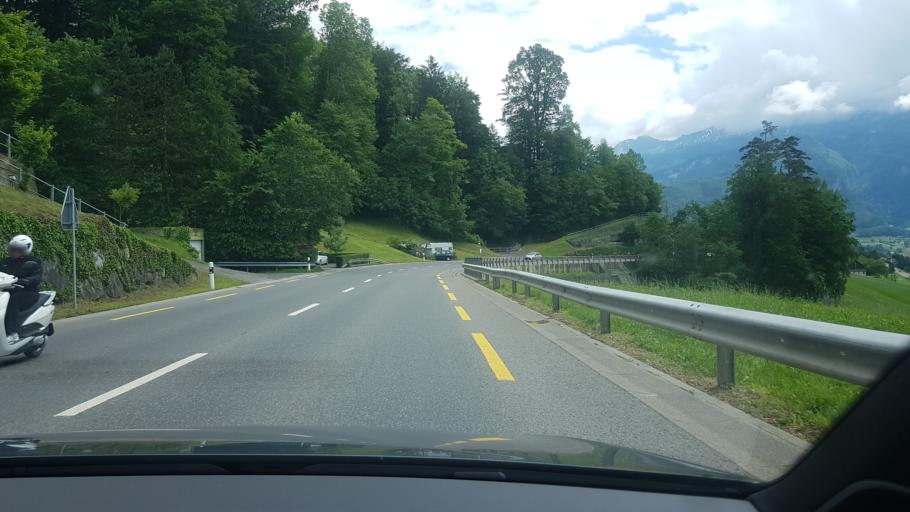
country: CH
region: Schwyz
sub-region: Bezirk Schwyz
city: Schwyz
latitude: 47.0404
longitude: 8.6395
